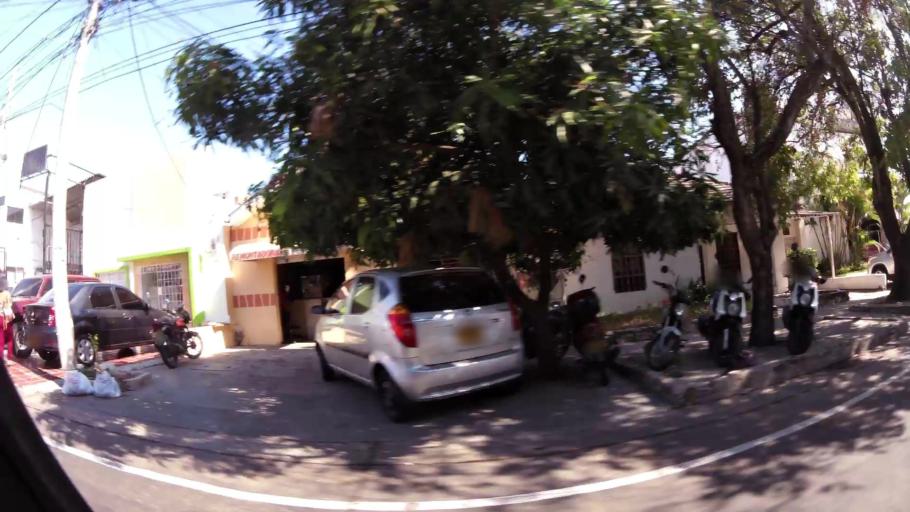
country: CO
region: Atlantico
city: Barranquilla
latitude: 10.9937
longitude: -74.8024
